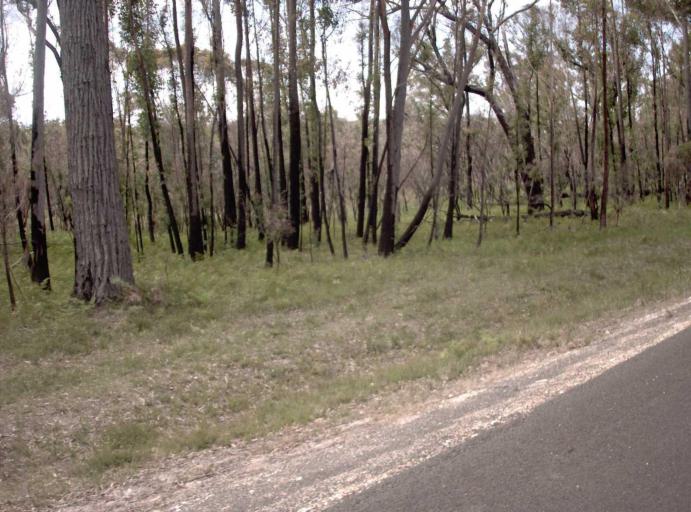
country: AU
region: New South Wales
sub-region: Bega Valley
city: Eden
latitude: -37.5150
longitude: 149.5030
